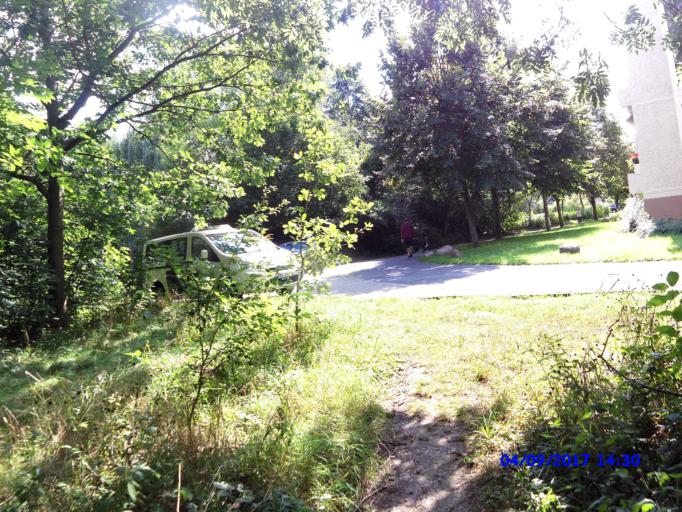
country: DE
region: Saxony
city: Taucha
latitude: 51.3576
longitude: 12.4652
